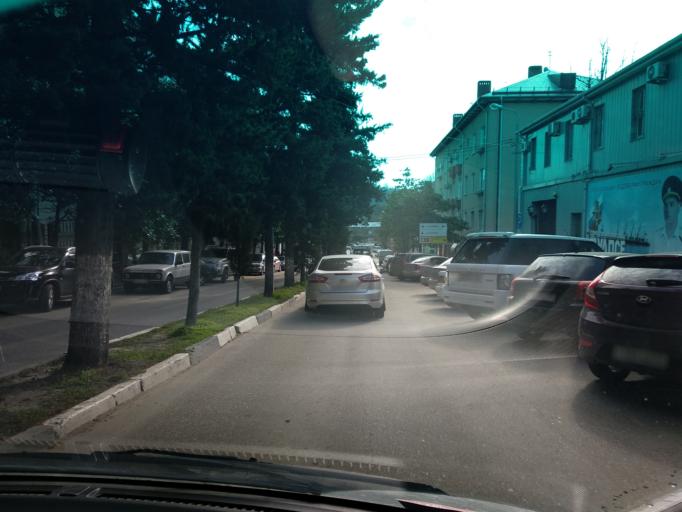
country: RU
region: Krasnodarskiy
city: Tuapse
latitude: 44.0979
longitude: 39.0752
